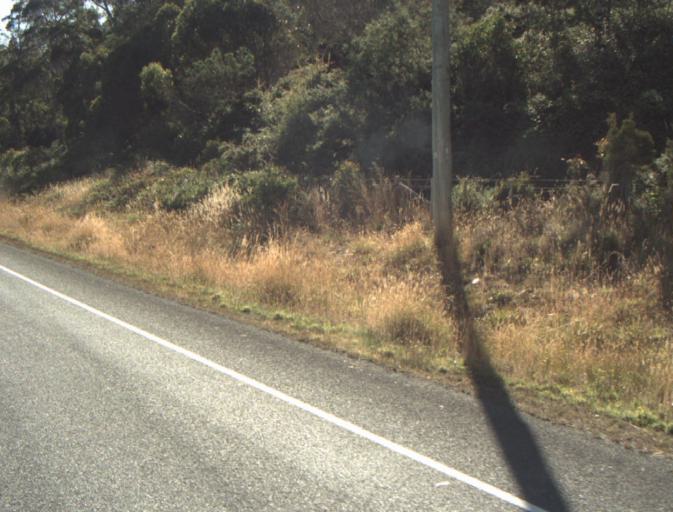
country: AU
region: Tasmania
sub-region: Launceston
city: Newstead
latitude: -41.4051
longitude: 147.2829
